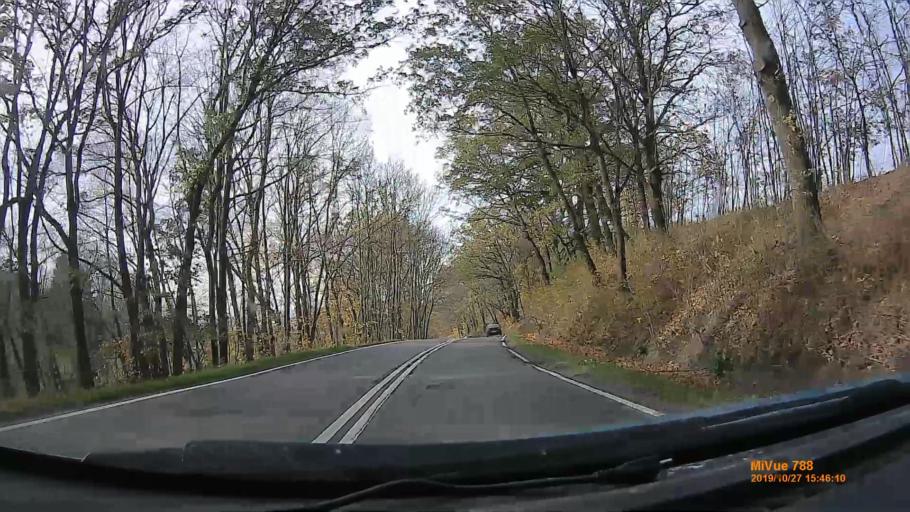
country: PL
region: Lower Silesian Voivodeship
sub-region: Powiat klodzki
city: Bozkow
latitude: 50.4800
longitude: 16.5879
